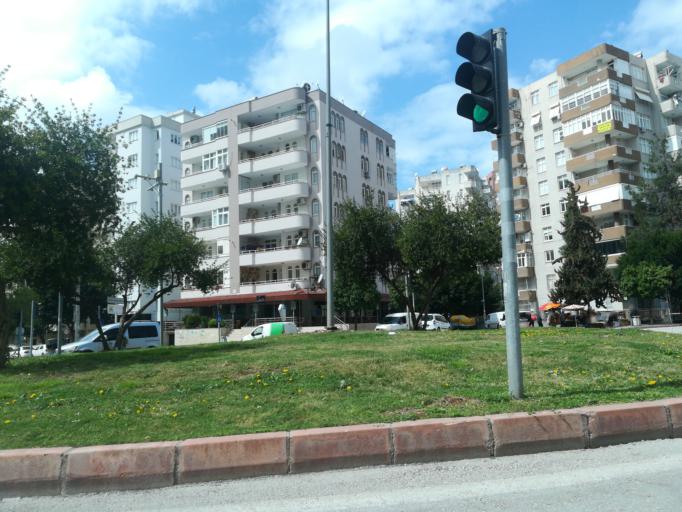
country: TR
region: Adana
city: Adana
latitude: 37.0395
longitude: 35.3027
